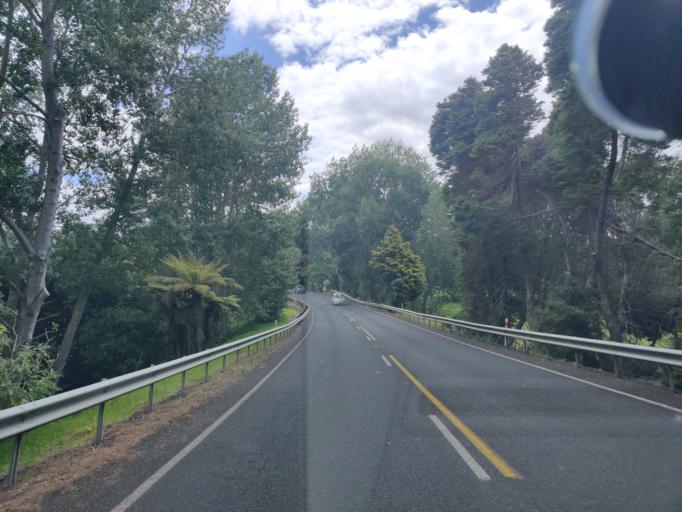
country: NZ
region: Northland
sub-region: Far North District
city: Kerikeri
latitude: -35.2914
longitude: 173.9955
